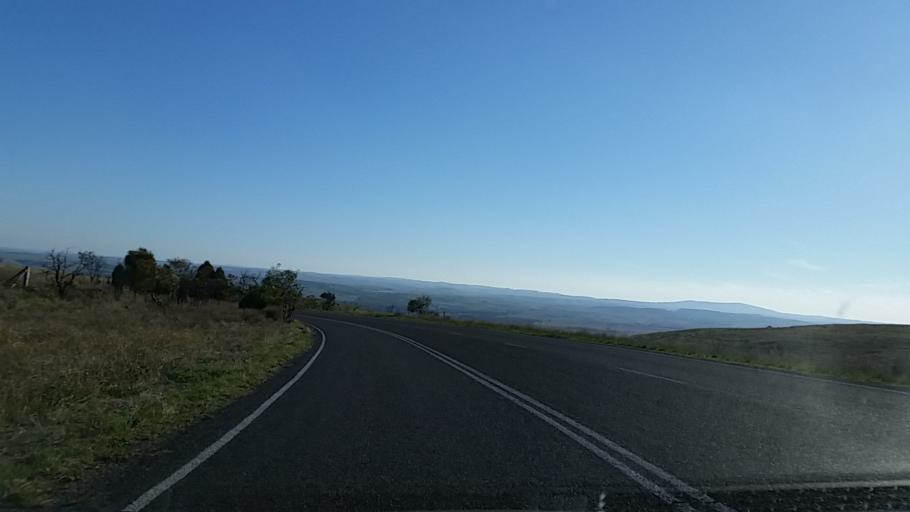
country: AU
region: South Australia
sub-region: Mount Barker
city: Callington
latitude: -35.1111
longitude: 139.0755
